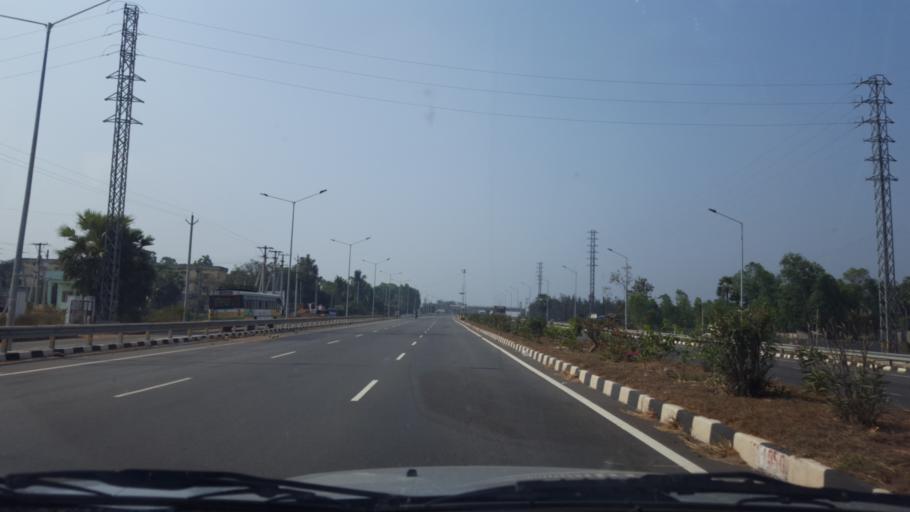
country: IN
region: Andhra Pradesh
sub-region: Vishakhapatnam
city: Bhimunipatnam
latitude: 17.9995
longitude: 83.4756
